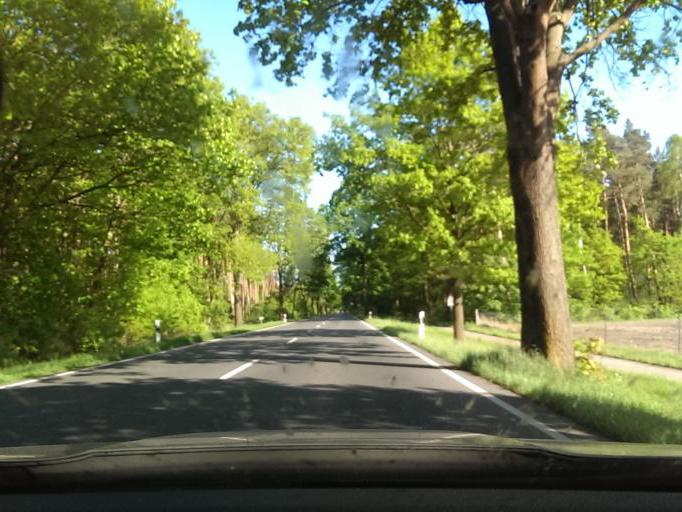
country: DE
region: Lower Saxony
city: Wietze
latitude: 52.6435
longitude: 9.8755
